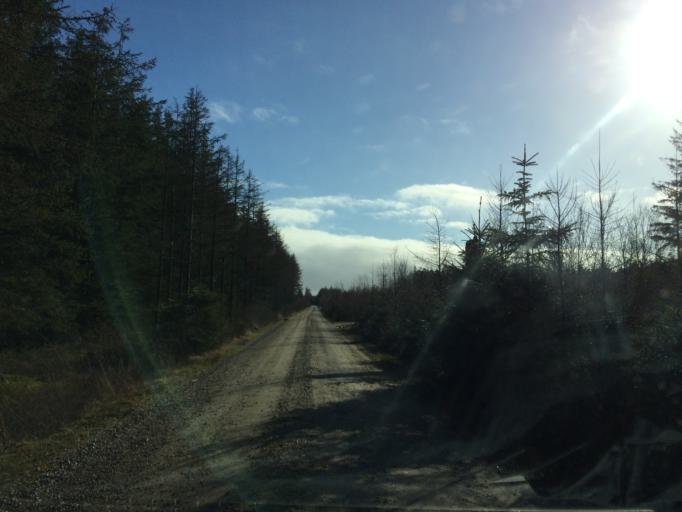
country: DK
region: Central Jutland
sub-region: Holstebro Kommune
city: Ulfborg
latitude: 56.2709
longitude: 8.3856
